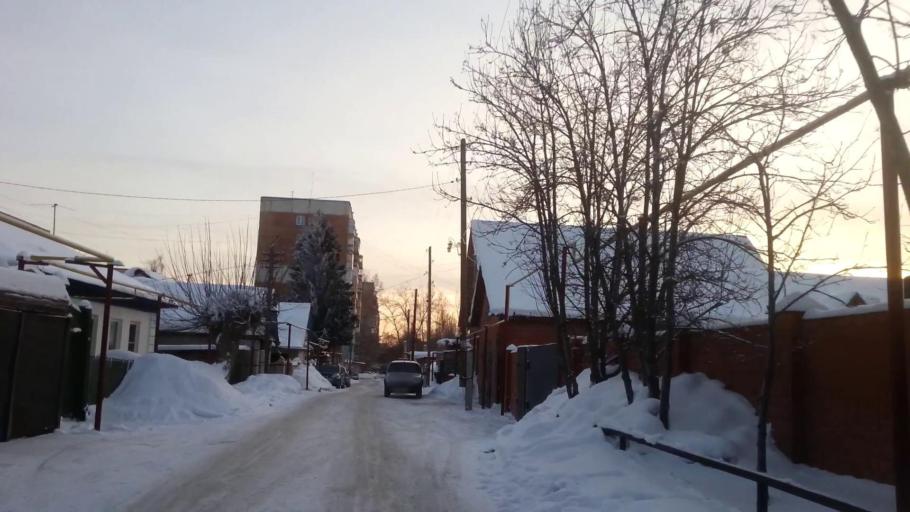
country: RU
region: Altai Krai
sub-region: Gorod Barnaulskiy
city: Barnaul
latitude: 53.3527
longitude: 83.6910
